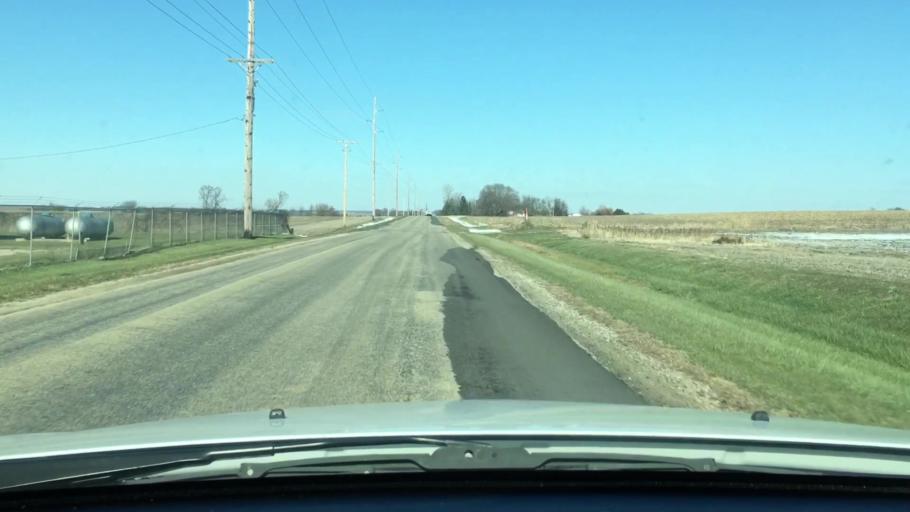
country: US
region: Illinois
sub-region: Ogle County
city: Hillcrest
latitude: 41.9378
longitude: -89.0004
